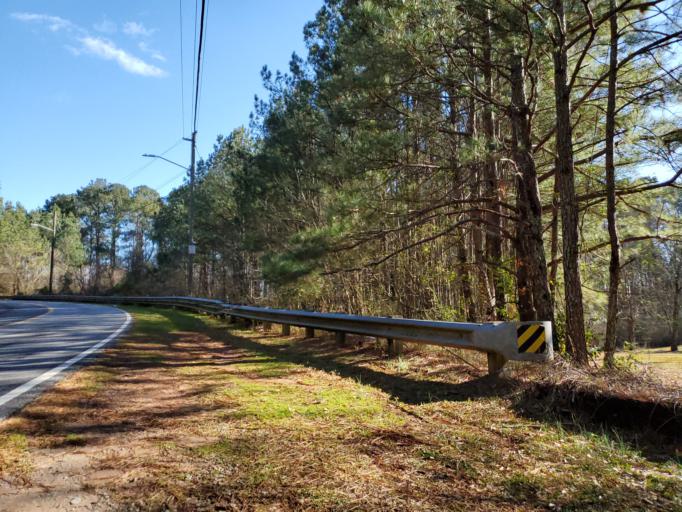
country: US
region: Georgia
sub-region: DeKalb County
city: Stone Mountain
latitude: 33.7731
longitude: -84.1955
